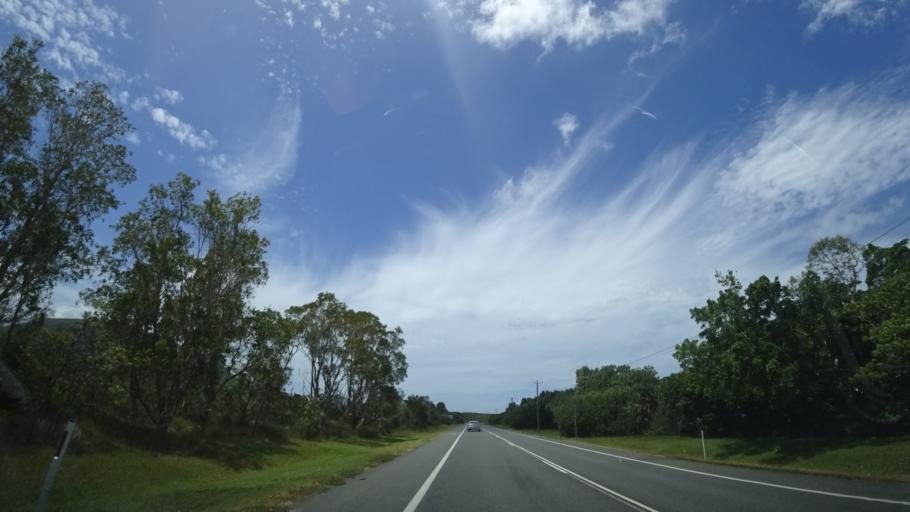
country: AU
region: Queensland
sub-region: Sunshine Coast
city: Coolum Beach
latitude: -26.5751
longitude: 153.0913
